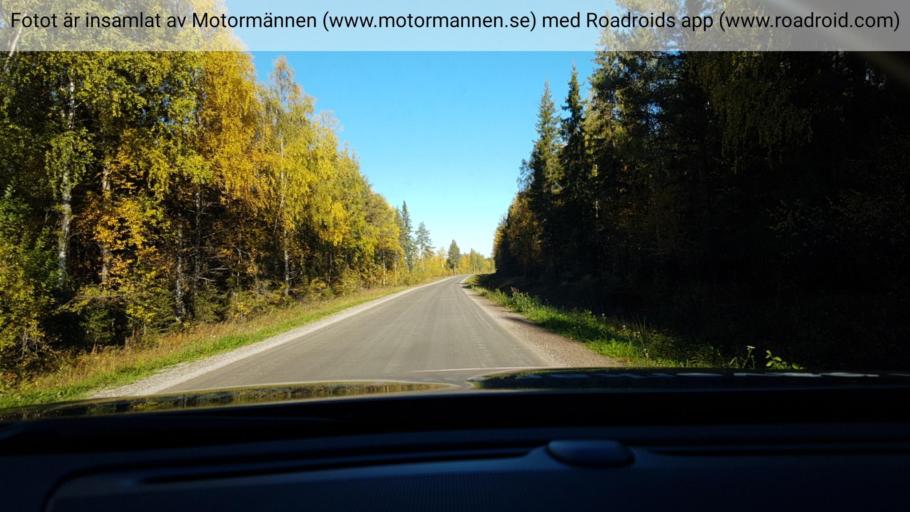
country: SE
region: Norrbotten
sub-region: Alvsbyns Kommun
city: AElvsbyn
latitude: 66.2578
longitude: 21.1406
